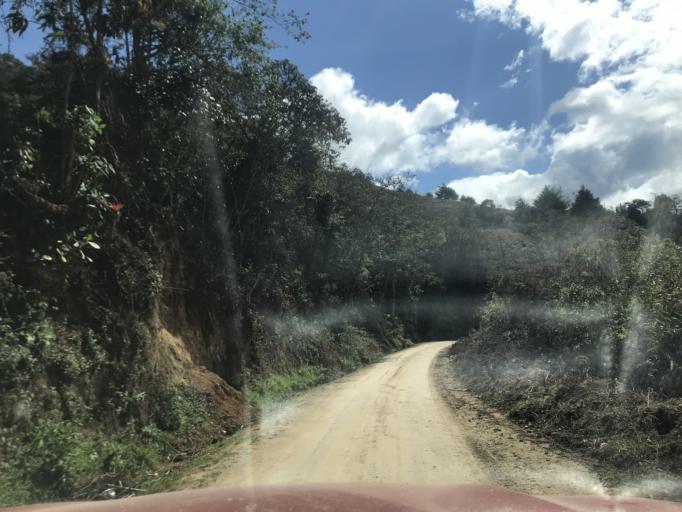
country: PE
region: Cajamarca
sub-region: Provincia de Chota
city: Querocoto
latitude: -6.3509
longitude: -79.0406
